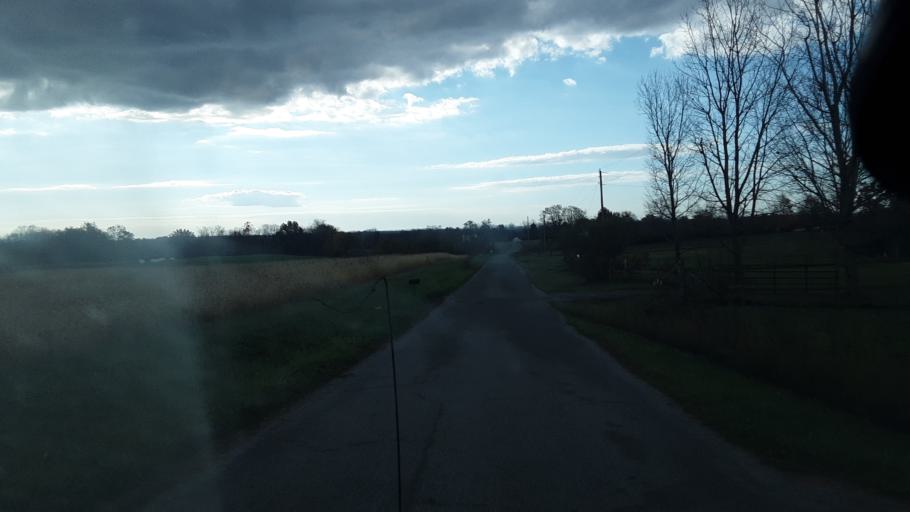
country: US
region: Ohio
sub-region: Highland County
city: Leesburg
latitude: 39.3510
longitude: -83.4760
